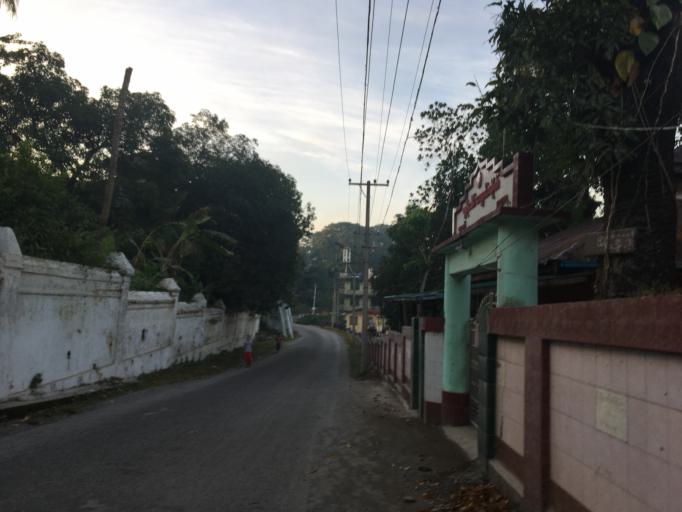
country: MM
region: Mon
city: Mawlamyine
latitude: 16.4890
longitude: 97.6279
